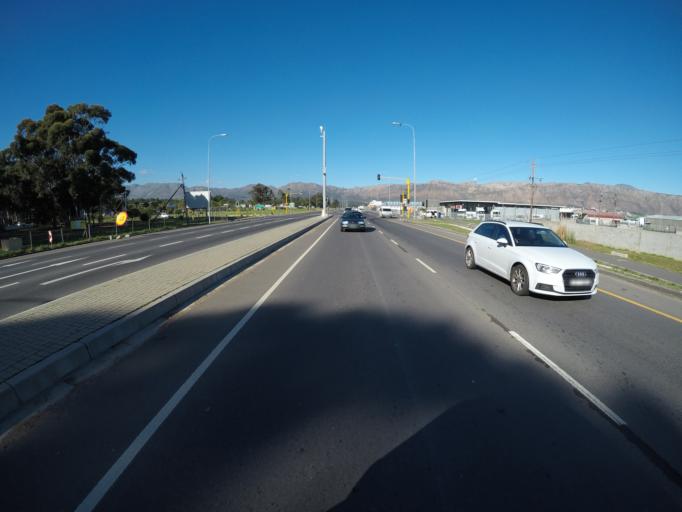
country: ZA
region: Western Cape
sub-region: Overberg District Municipality
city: Grabouw
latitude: -34.1171
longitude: 18.8756
